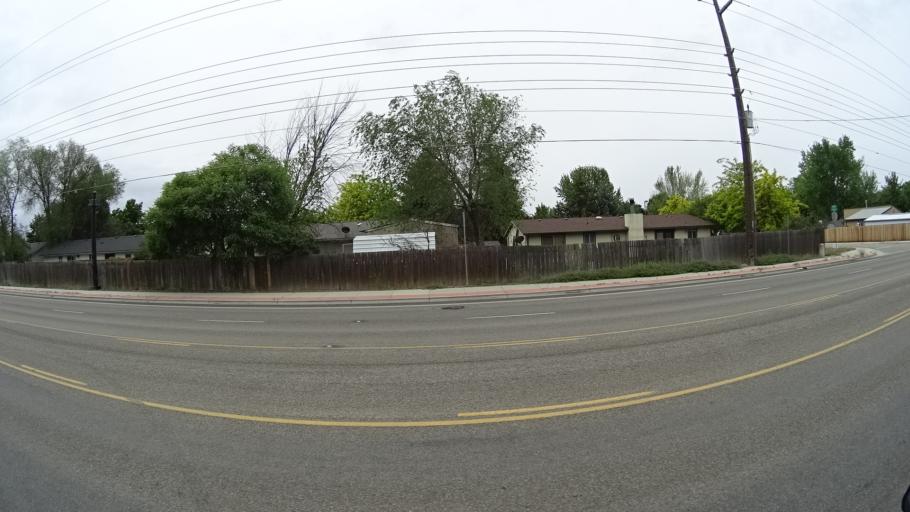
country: US
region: Idaho
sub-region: Ada County
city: Garden City
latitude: 43.6337
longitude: -116.3076
